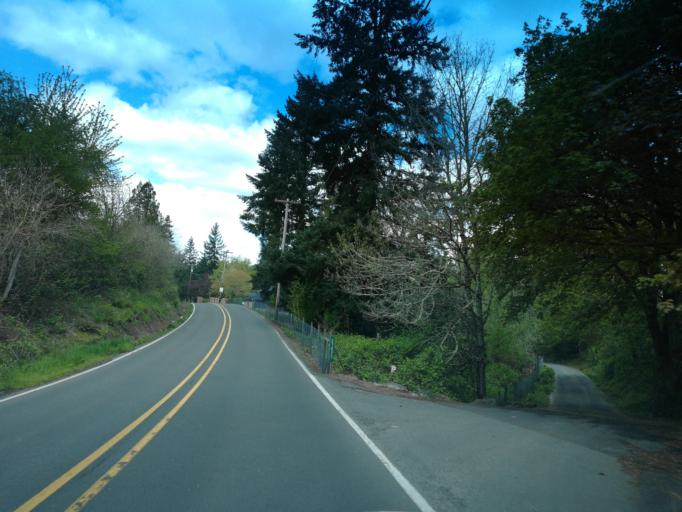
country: US
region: Oregon
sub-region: Clackamas County
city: Damascus
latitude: 45.4339
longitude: -122.4392
